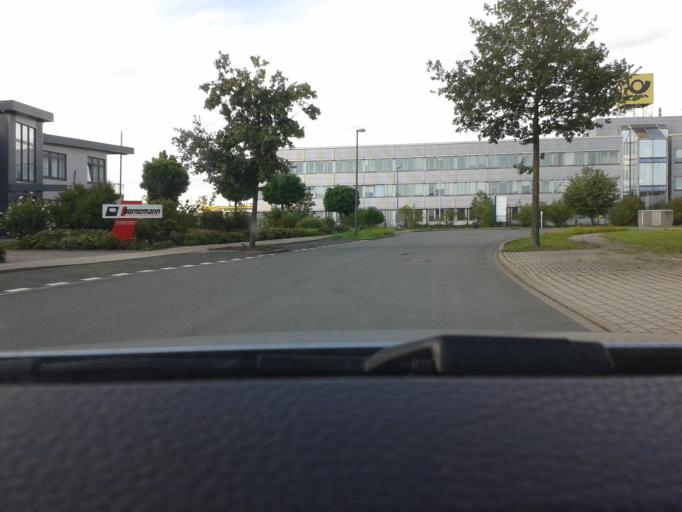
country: DE
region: North Rhine-Westphalia
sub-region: Regierungsbezirk Dusseldorf
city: Hochfeld
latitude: 51.4295
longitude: 6.6928
